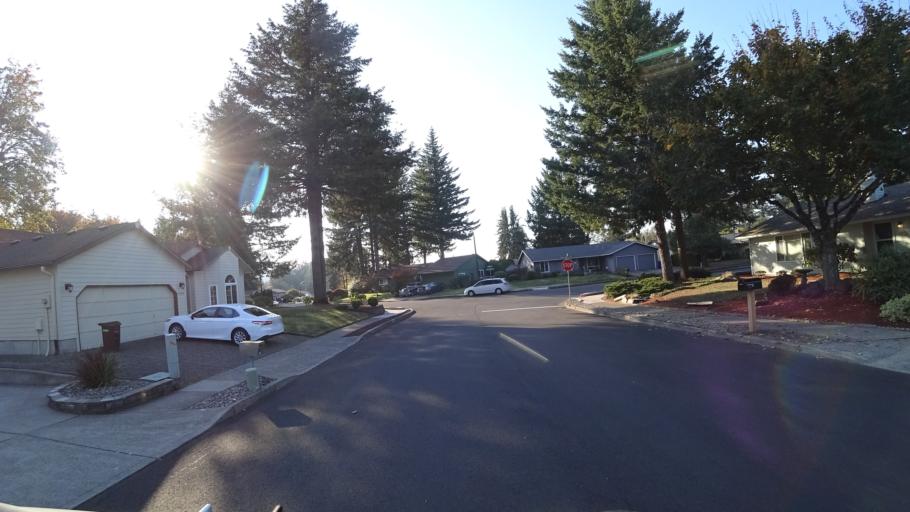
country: US
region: Oregon
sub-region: Multnomah County
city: Gresham
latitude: 45.5077
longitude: -122.4476
